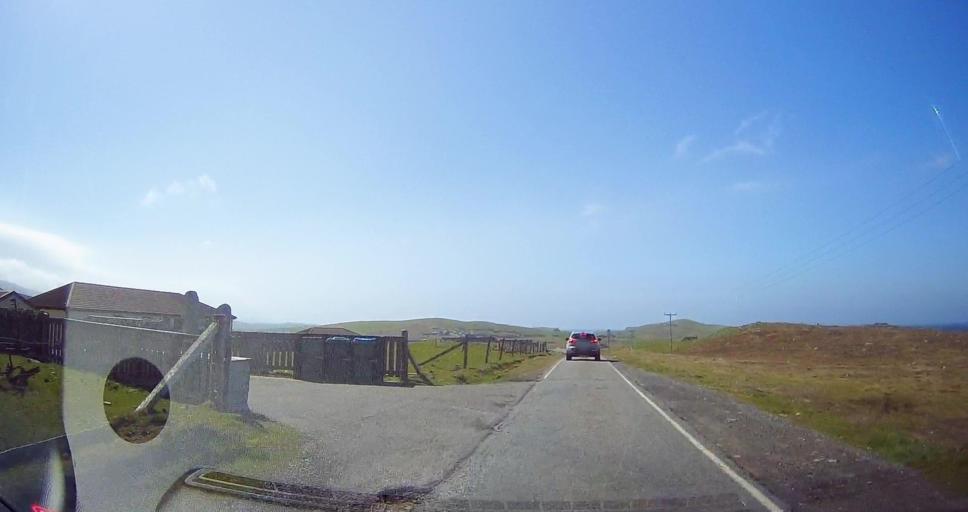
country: GB
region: Scotland
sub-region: Shetland Islands
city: Sandwick
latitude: 60.0893
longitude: -1.3271
